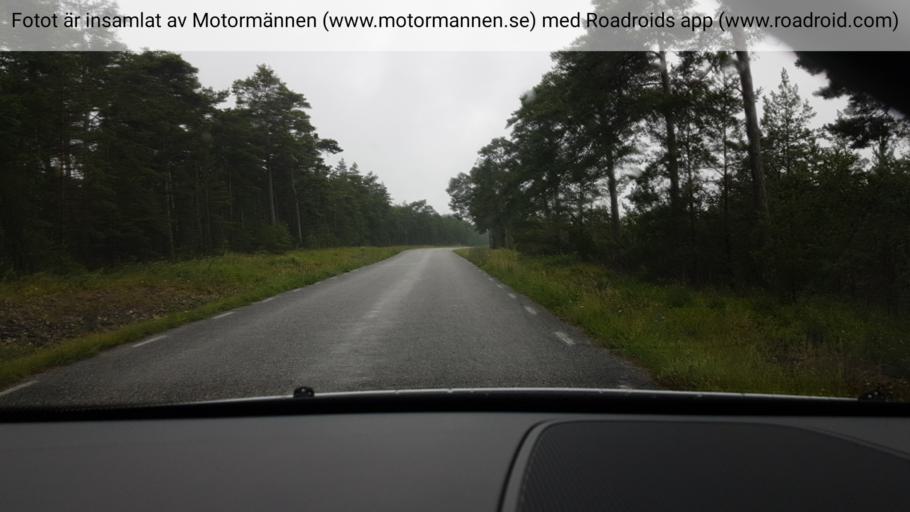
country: SE
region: Gotland
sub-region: Gotland
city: Slite
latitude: 57.8592
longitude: 18.8264
